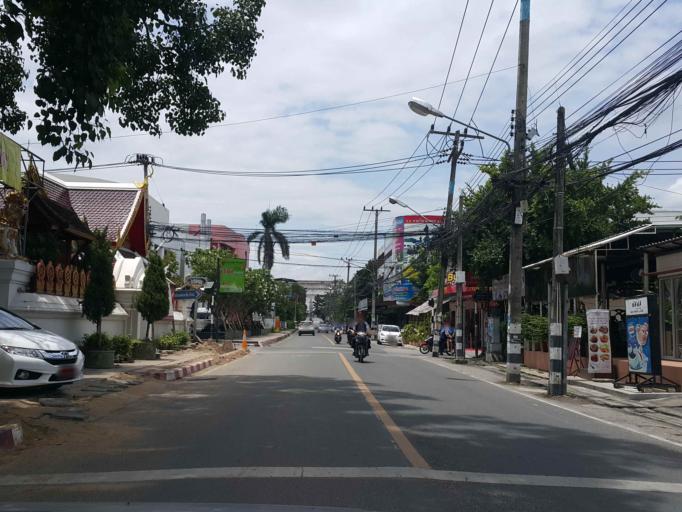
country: TH
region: Chiang Mai
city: Chiang Mai
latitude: 18.7928
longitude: 98.9820
